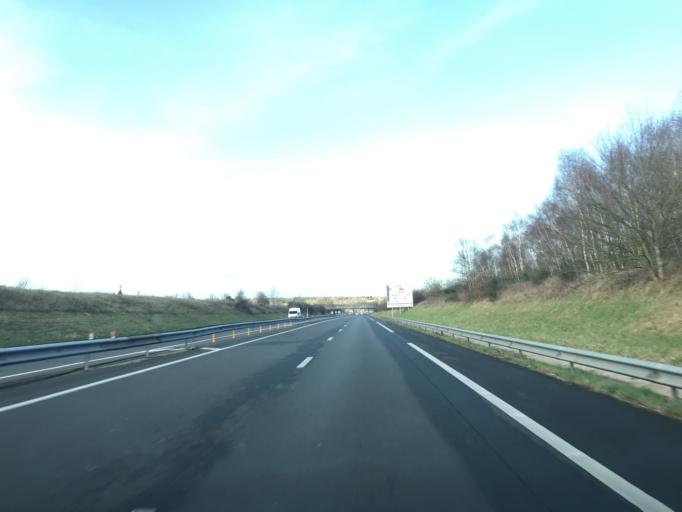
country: FR
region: Pays de la Loire
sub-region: Departement de Maine-et-Loire
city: Durtal
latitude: 47.6396
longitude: -0.2743
